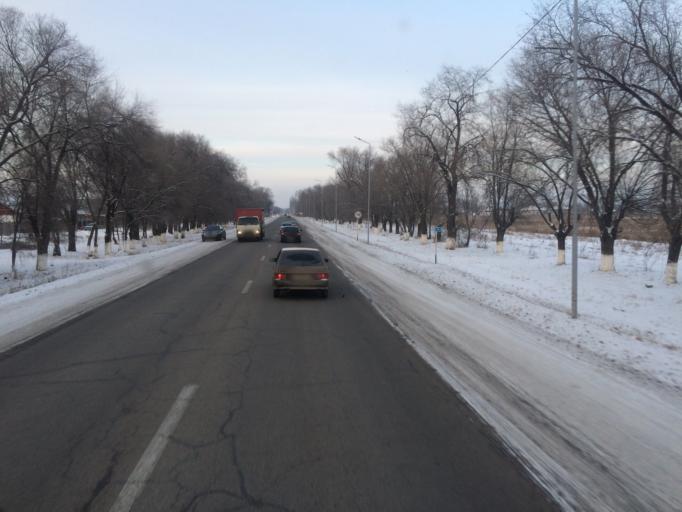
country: KZ
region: Almaty Oblysy
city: Burunday
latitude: 43.2631
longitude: 76.6697
